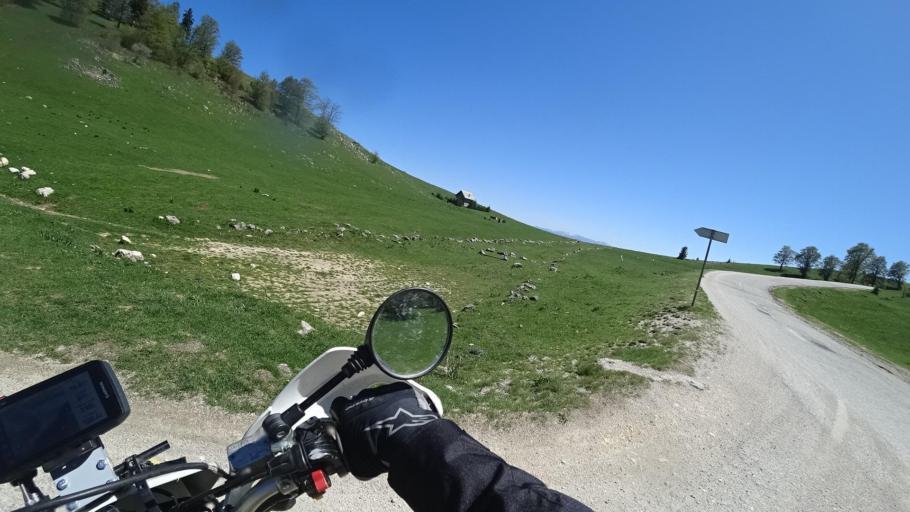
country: BA
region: Federation of Bosnia and Herzegovina
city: Turbe
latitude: 44.2778
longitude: 17.6064
